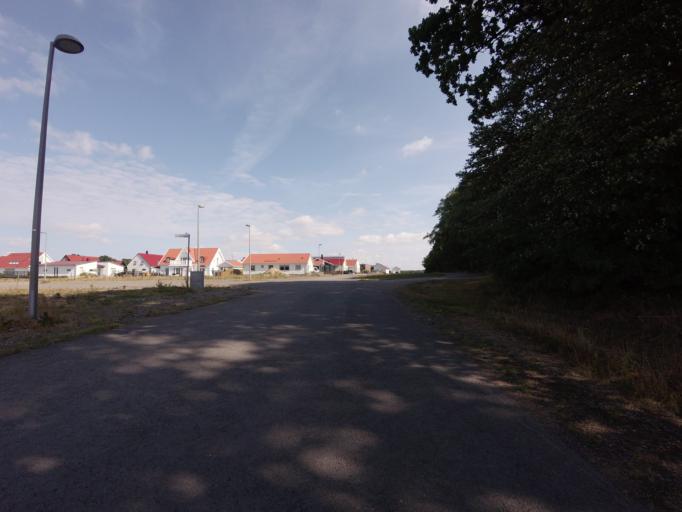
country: SE
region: Skane
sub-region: Helsingborg
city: Odakra
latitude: 56.0794
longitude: 12.7112
